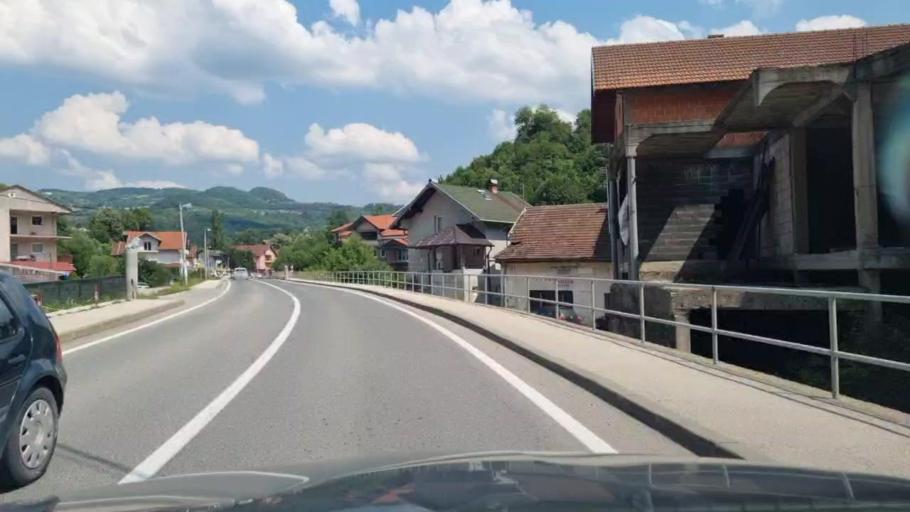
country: BA
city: Stupari
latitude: 44.3118
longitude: 18.6810
